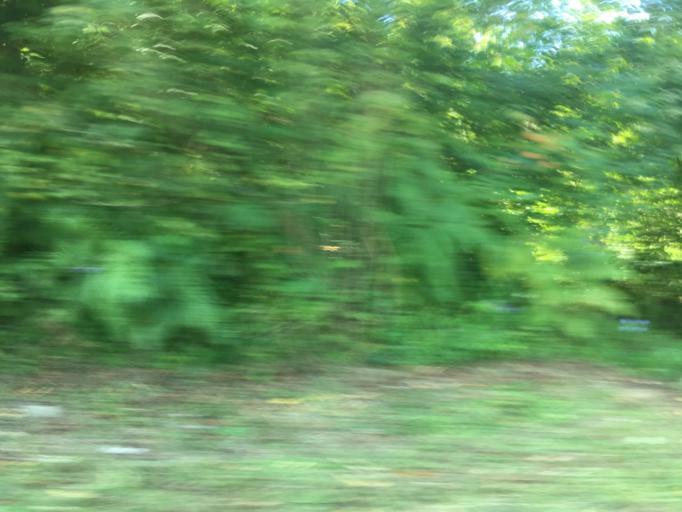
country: SI
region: Metlika
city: Metlika
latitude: 45.6080
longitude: 15.3308
